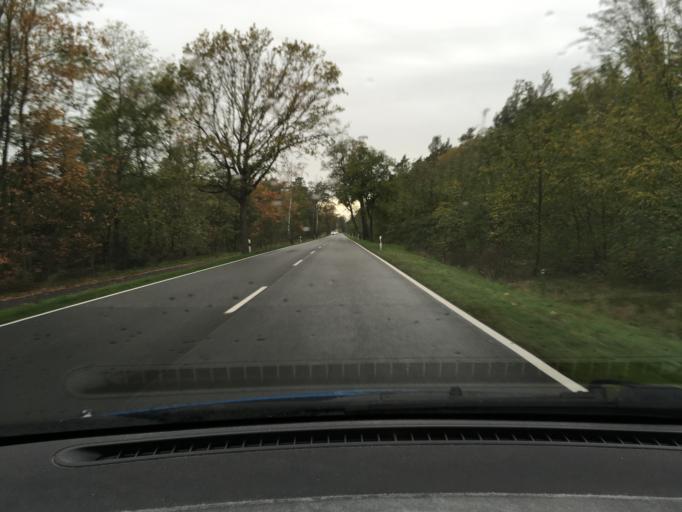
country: DE
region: Saxony-Anhalt
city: Rodleben
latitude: 51.9176
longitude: 12.1774
